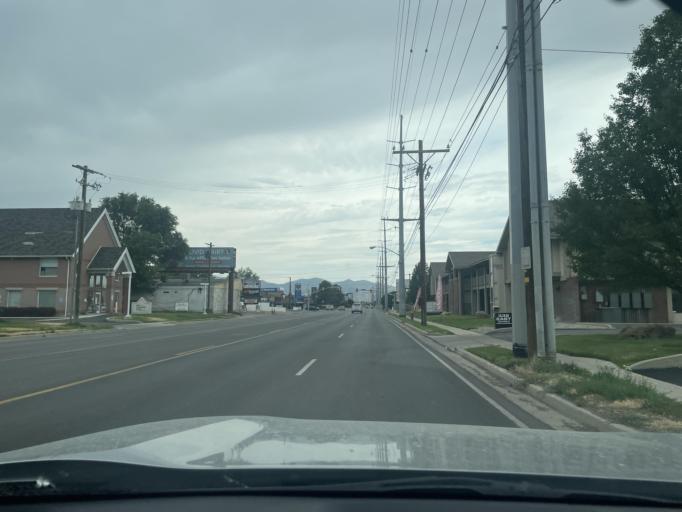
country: US
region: Utah
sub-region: Salt Lake County
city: Millcreek
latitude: 40.6871
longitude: -111.8809
